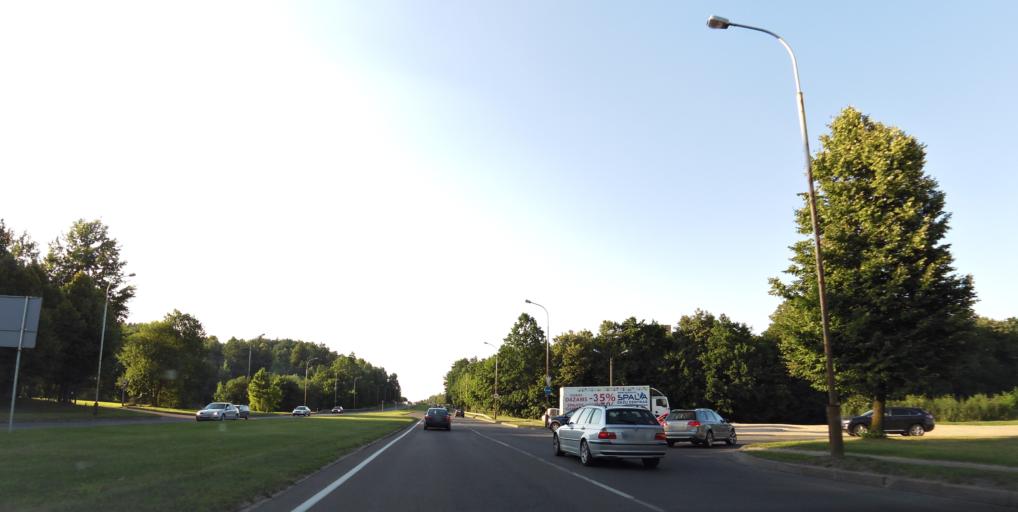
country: LT
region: Vilnius County
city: Seskine
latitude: 54.7227
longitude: 25.2700
